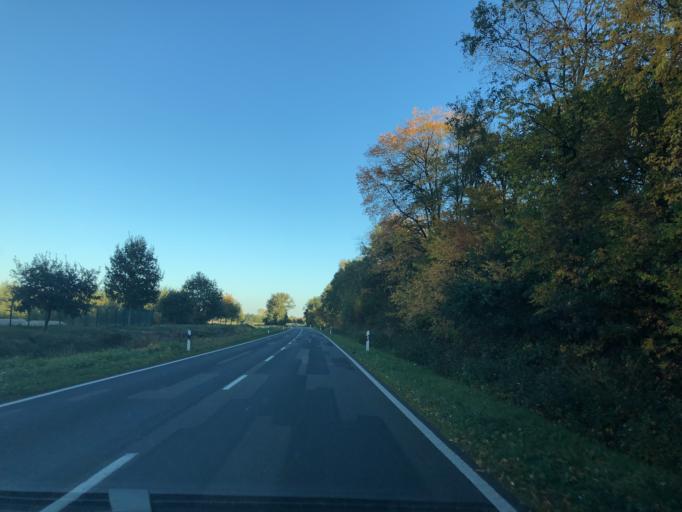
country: DE
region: Lower Saxony
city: Friesoythe
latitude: 53.0290
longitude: 7.7771
